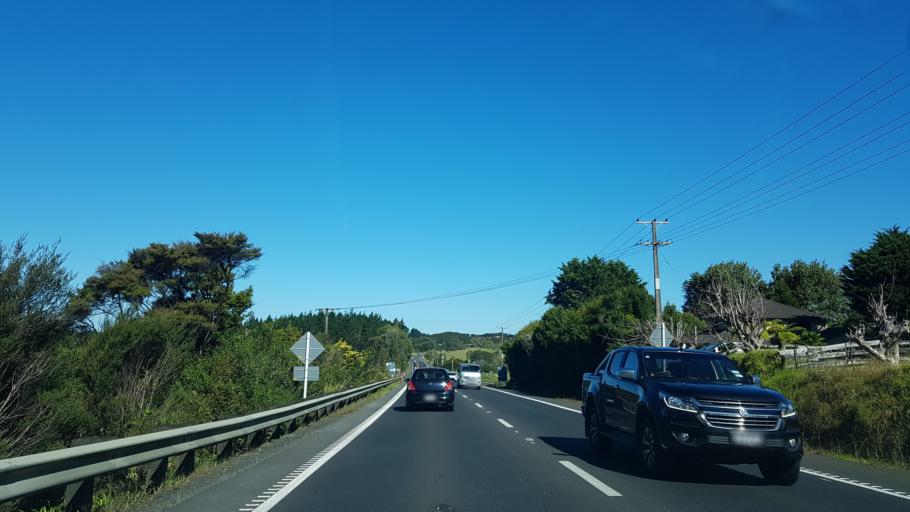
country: NZ
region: Auckland
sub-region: Auckland
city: Warkworth
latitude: -36.4718
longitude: 174.6493
